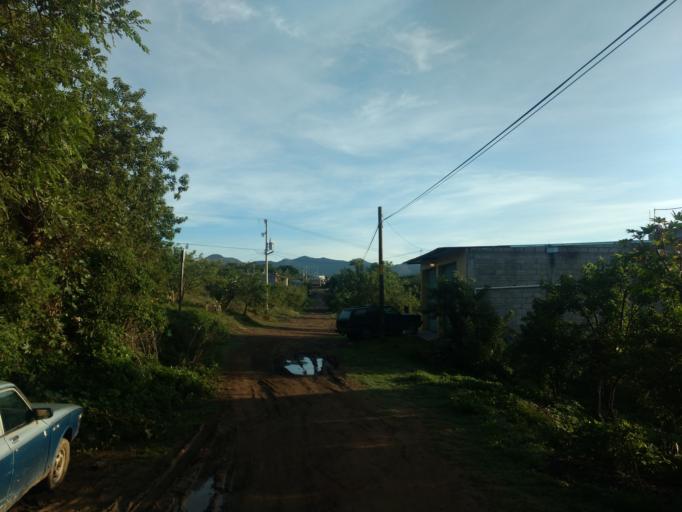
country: MX
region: Oaxaca
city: Ciudad de Huajuapam de Leon
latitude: 17.8319
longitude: -97.7871
